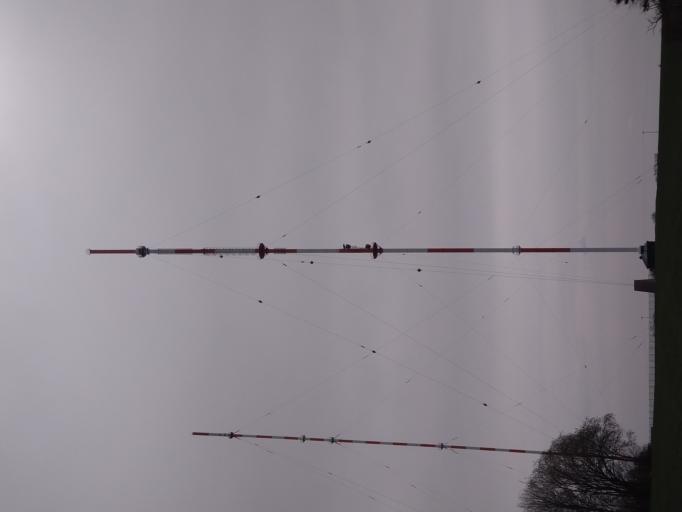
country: DE
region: Bavaria
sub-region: Upper Palatinate
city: Postbauer-Heng
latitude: 49.3256
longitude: 11.3762
